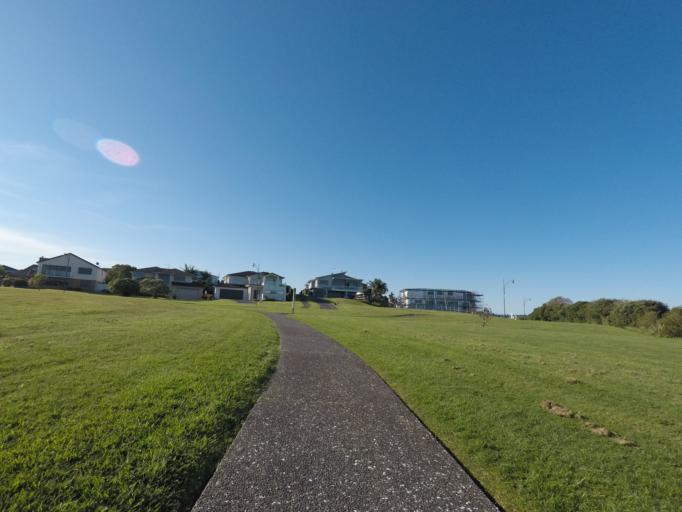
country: NZ
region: Auckland
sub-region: Auckland
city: Rosebank
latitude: -36.8368
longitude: 174.6612
